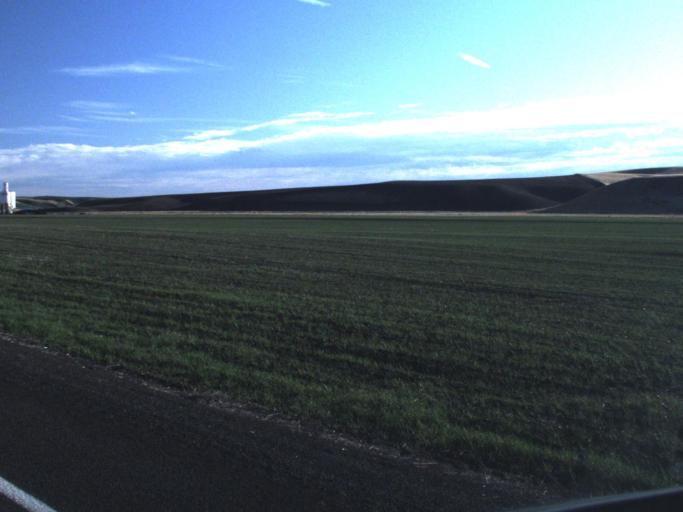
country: US
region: Washington
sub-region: Whitman County
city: Colfax
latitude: 46.8050
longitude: -117.6611
